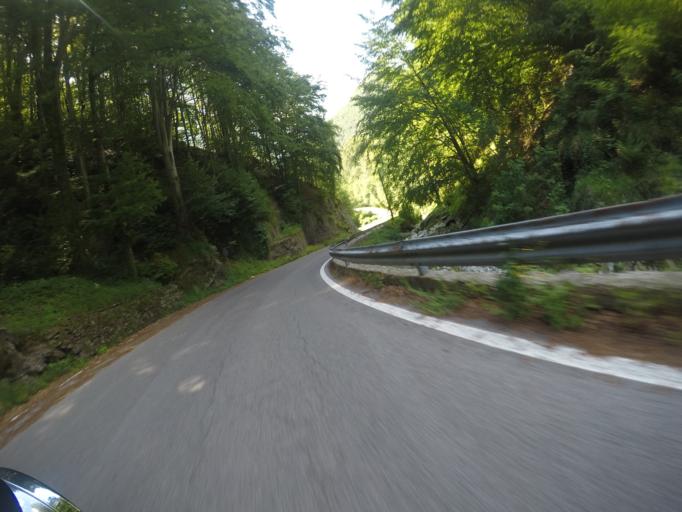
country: IT
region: Tuscany
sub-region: Provincia di Lucca
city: Fontana delle Monache
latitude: 44.0630
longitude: 10.2509
